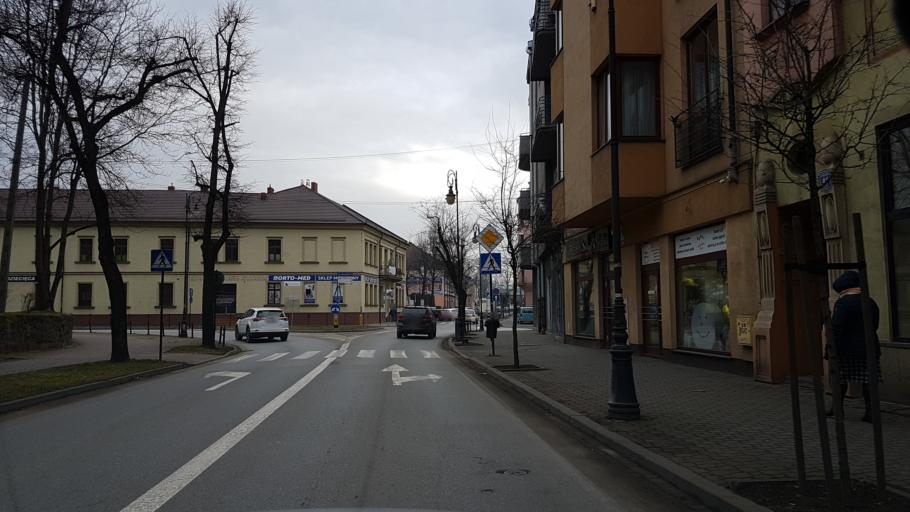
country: PL
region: Lesser Poland Voivodeship
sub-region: Powiat nowosadecki
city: Nowy Sacz
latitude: 49.6192
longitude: 20.6944
